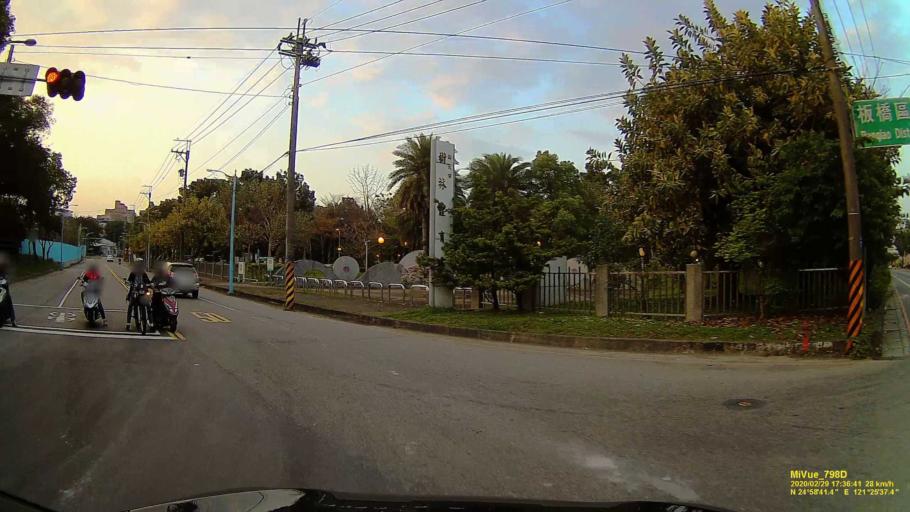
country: TW
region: Taipei
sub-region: Taipei
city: Banqiao
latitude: 24.9783
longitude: 121.4270
